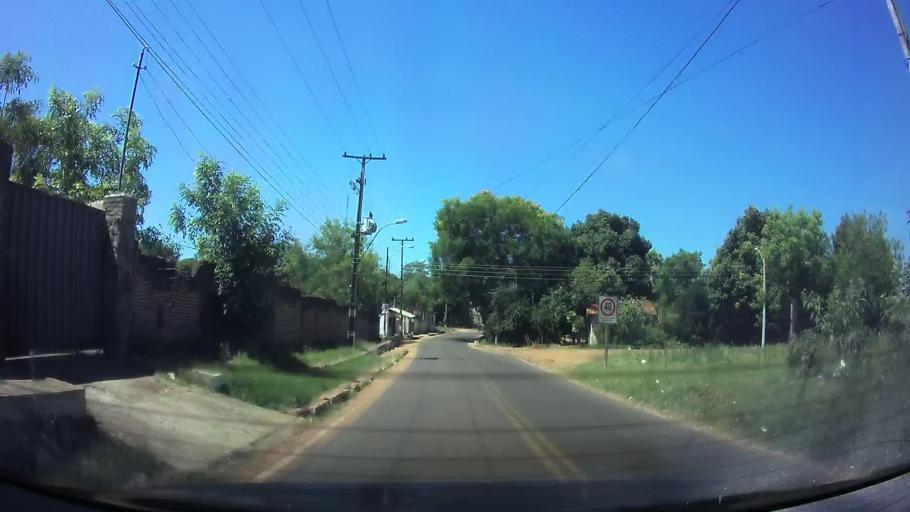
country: PY
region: Central
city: Aregua
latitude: -25.2969
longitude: -57.4153
